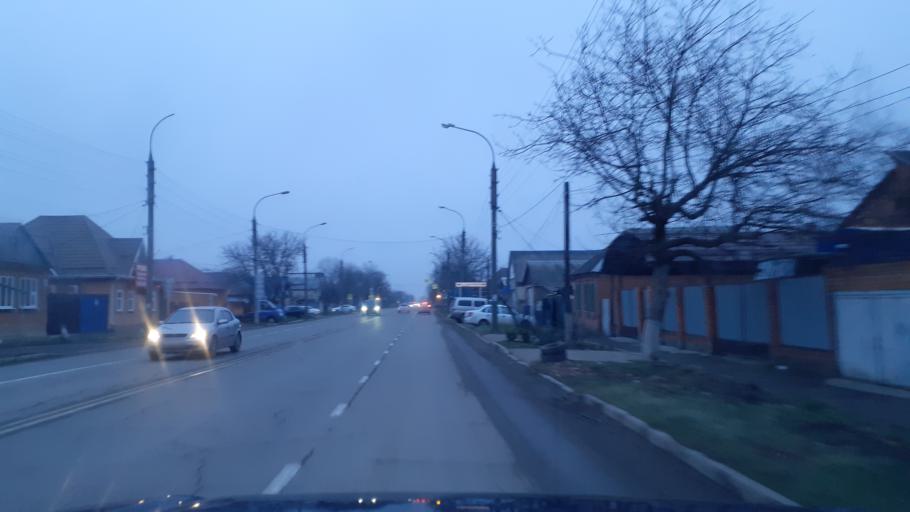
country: RU
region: Adygeya
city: Maykop
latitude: 44.6189
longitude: 40.0930
